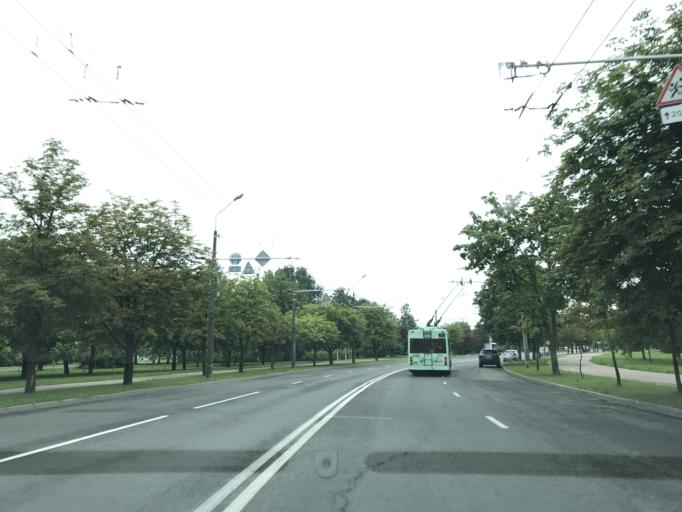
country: BY
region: Minsk
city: Borovlyany
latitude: 53.9492
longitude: 27.6408
